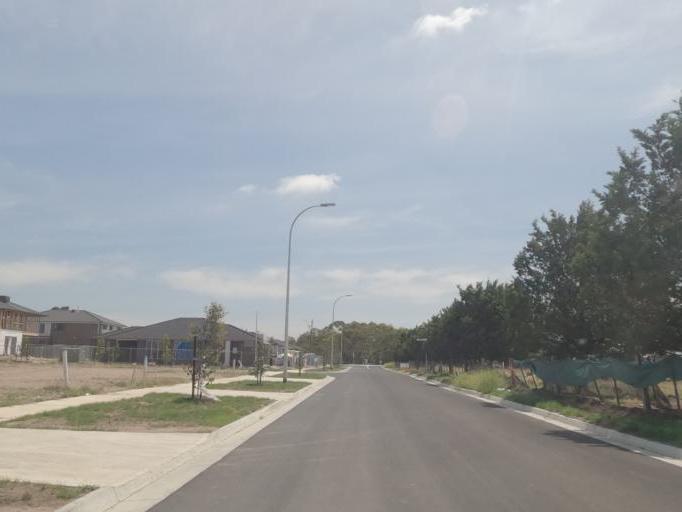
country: AU
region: Victoria
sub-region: Hume
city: Greenvale
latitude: -37.6356
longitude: 144.8757
